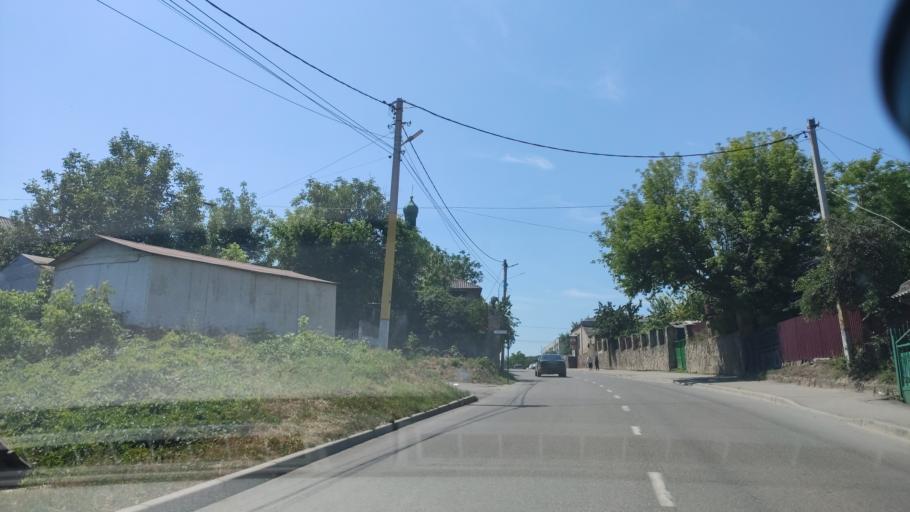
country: MD
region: Raionul Soroca
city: Soroca
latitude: 48.1633
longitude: 28.3022
